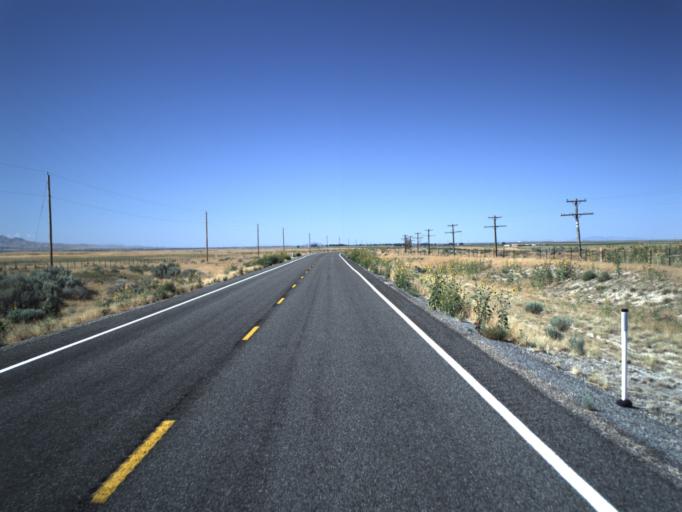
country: US
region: Utah
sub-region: Millard County
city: Delta
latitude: 39.5943
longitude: -112.3283
